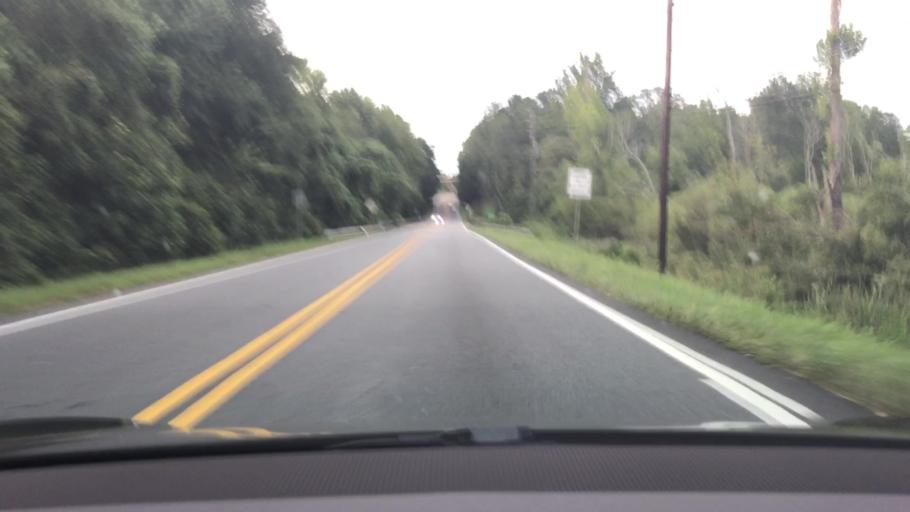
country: US
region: Georgia
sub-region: Gwinnett County
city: Suwanee
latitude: 34.0313
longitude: -84.0900
